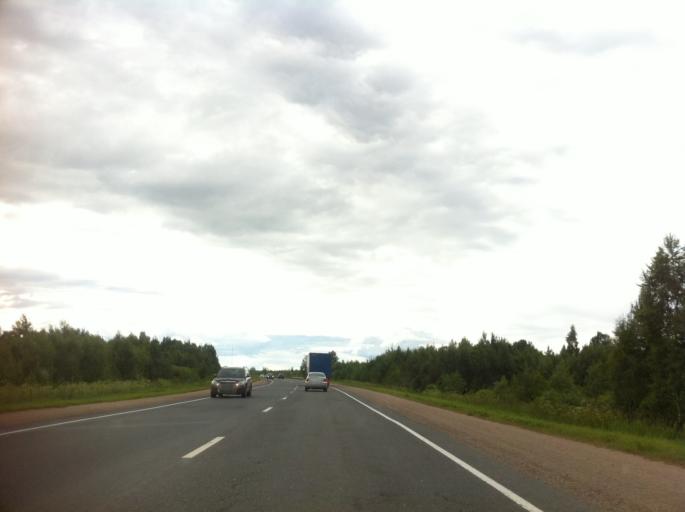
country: RU
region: Pskov
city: Pskov
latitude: 57.8554
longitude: 28.3743
